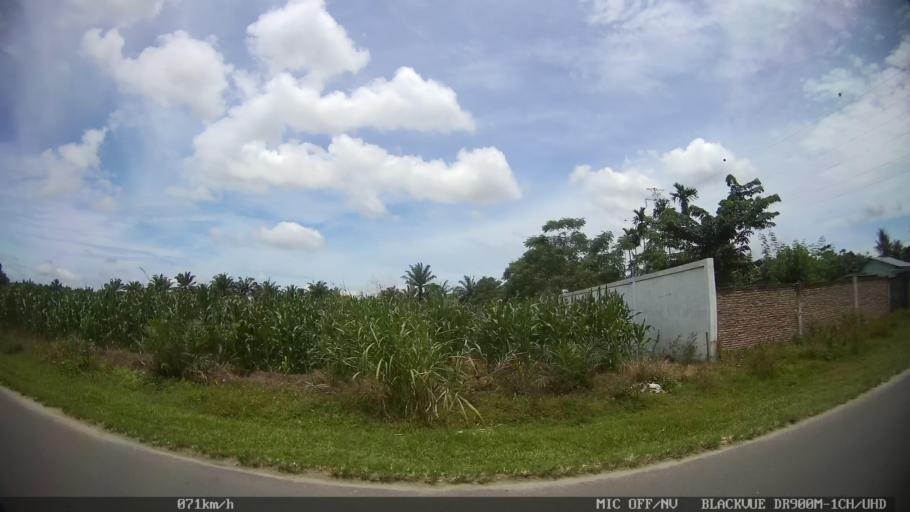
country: ID
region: North Sumatra
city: Percut
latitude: 3.5860
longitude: 98.8833
